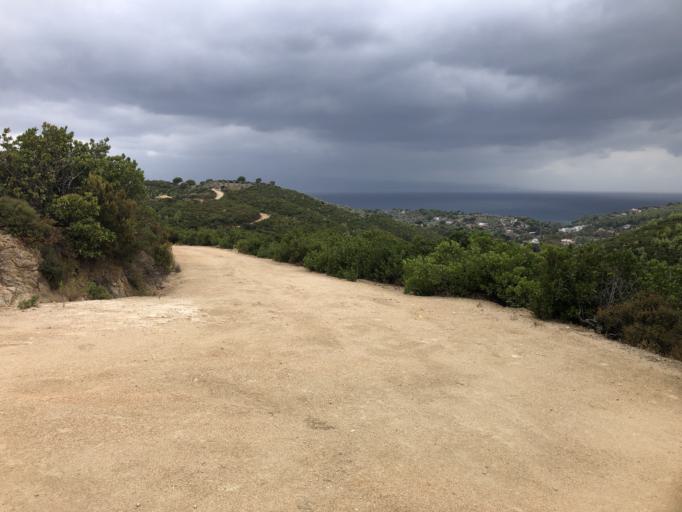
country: GR
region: Thessaly
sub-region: Nomos Magnisias
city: Skiathos
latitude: 39.1500
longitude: 23.4347
